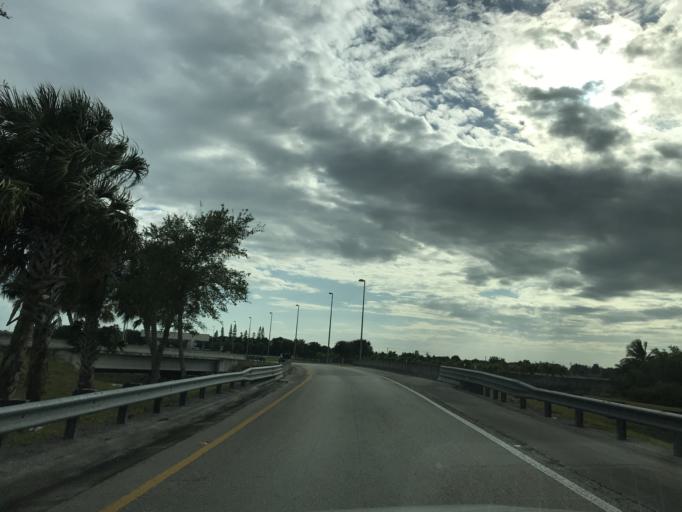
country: US
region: Florida
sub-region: Palm Beach County
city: Villages of Oriole
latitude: 26.4579
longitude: -80.1761
